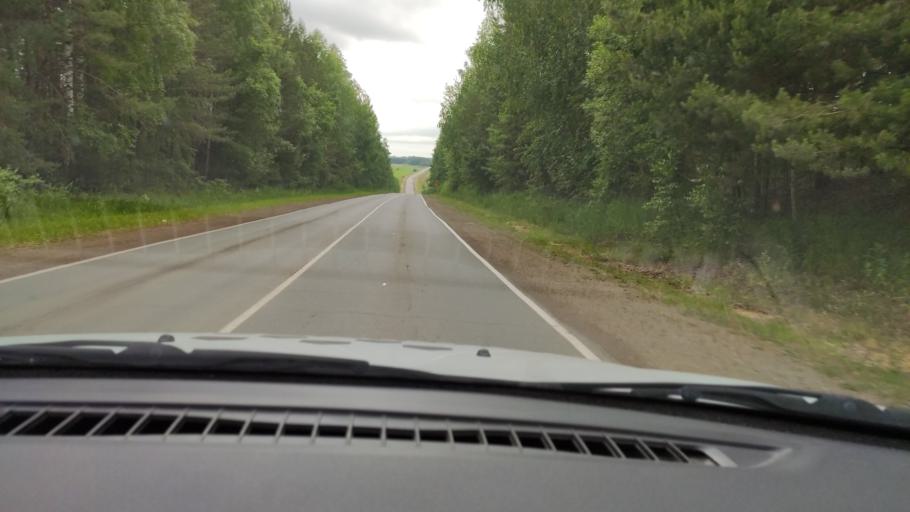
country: RU
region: Perm
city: Orda
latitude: 57.3300
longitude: 56.7063
